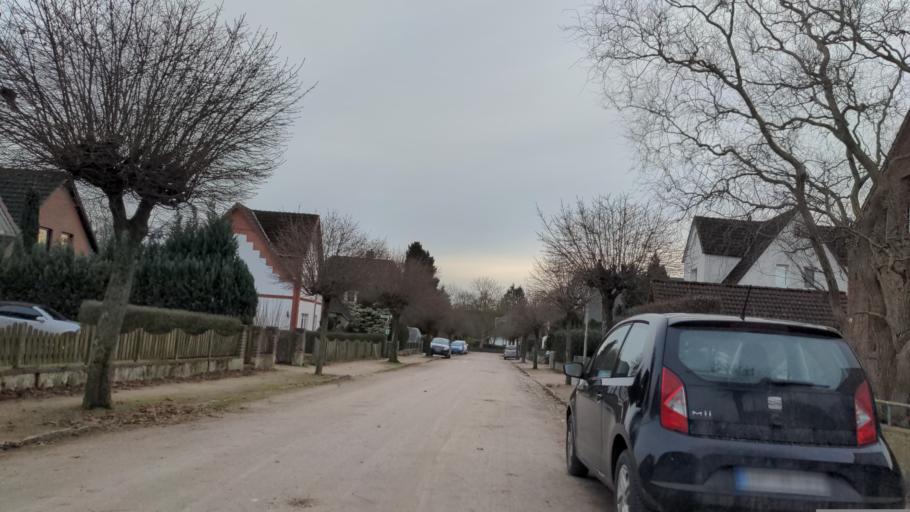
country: DE
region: Schleswig-Holstein
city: Malente
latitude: 54.1686
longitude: 10.5606
